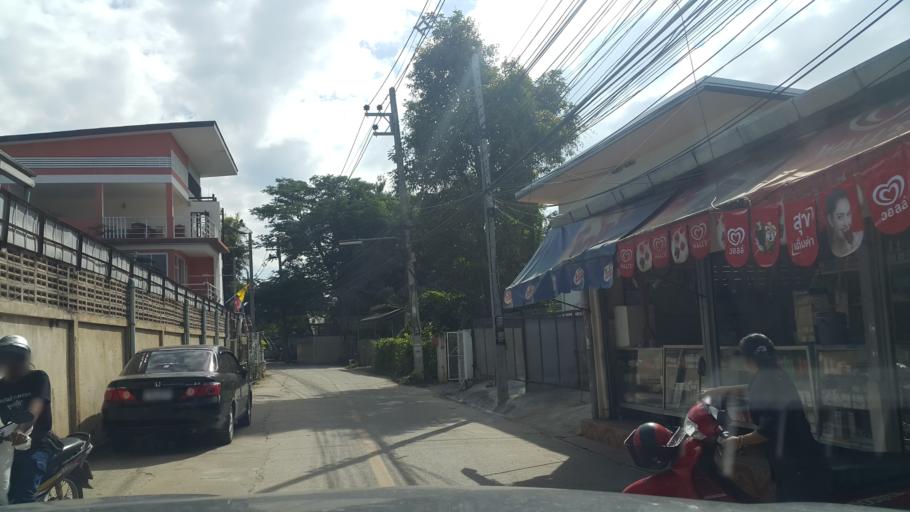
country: TH
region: Chiang Mai
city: Chiang Mai
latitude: 18.7810
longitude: 99.0212
